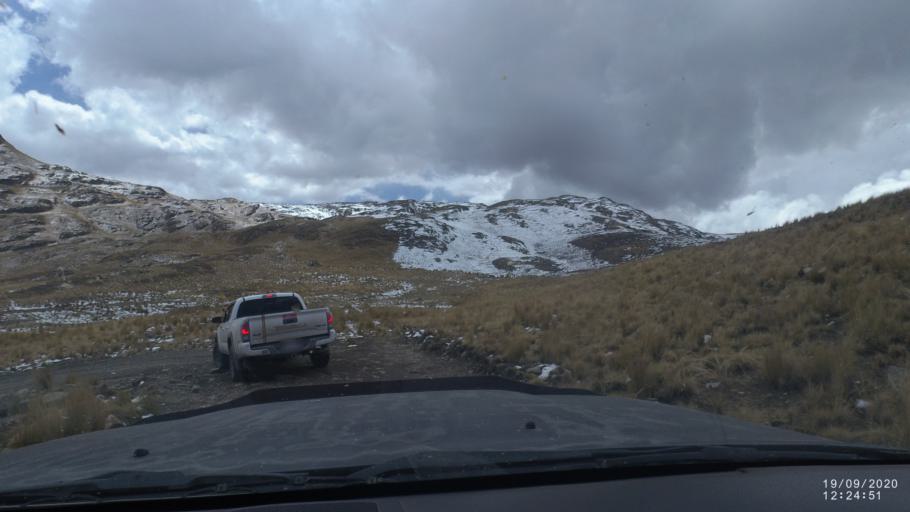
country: BO
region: Cochabamba
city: Cochabamba
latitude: -17.2936
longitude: -66.1101
